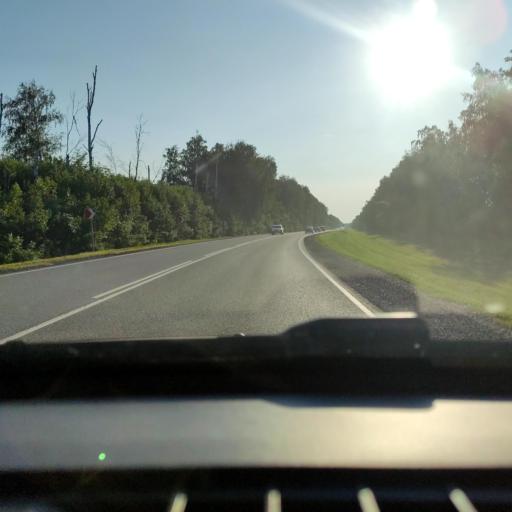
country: RU
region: Voronezj
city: Kashirskoye
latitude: 51.4585
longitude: 39.7684
